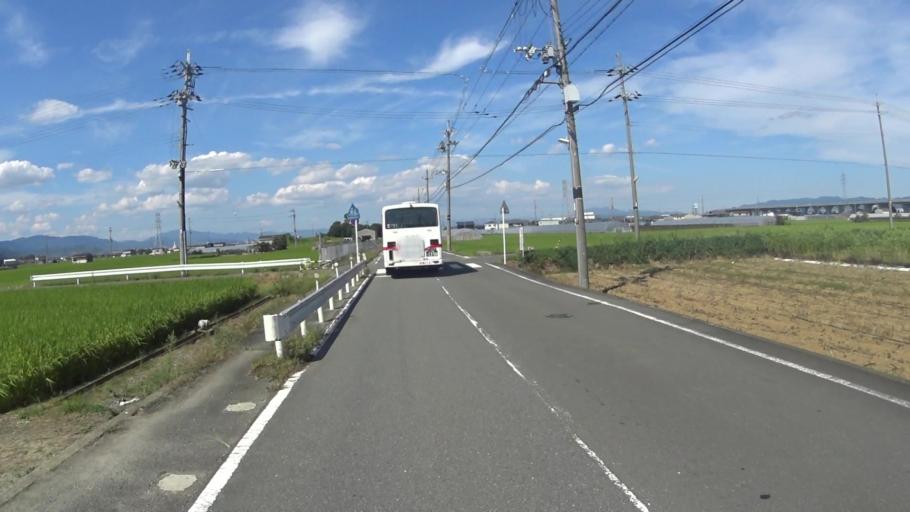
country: JP
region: Kyoto
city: Yawata
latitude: 34.8547
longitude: 135.7286
